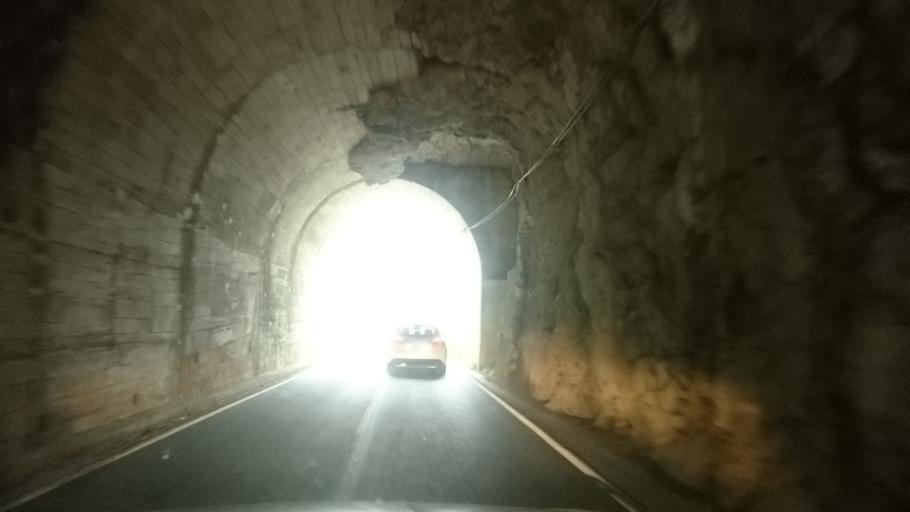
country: ES
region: Asturias
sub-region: Province of Asturias
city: Carrena
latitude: 43.2586
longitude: -4.8306
